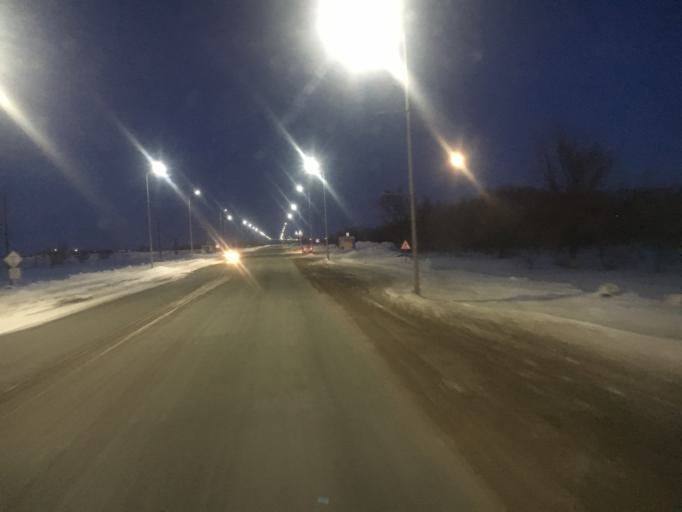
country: KZ
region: Batys Qazaqstan
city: Oral
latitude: 51.1578
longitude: 51.4997
